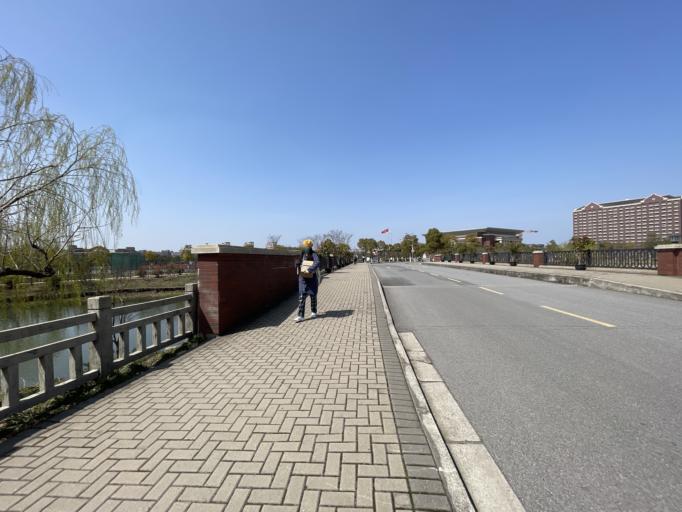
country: CN
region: Shanghai Shi
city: Shuyuan
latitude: 30.8926
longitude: 121.8859
